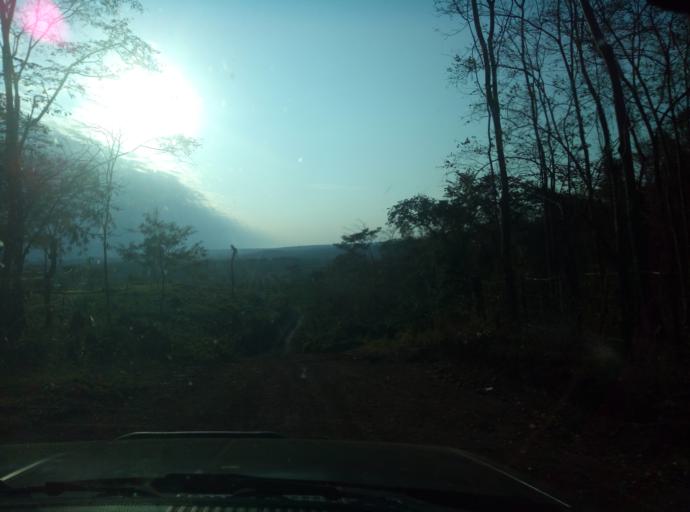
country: PY
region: Caaguazu
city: Doctor Cecilio Baez
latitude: -25.1987
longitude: -56.1337
